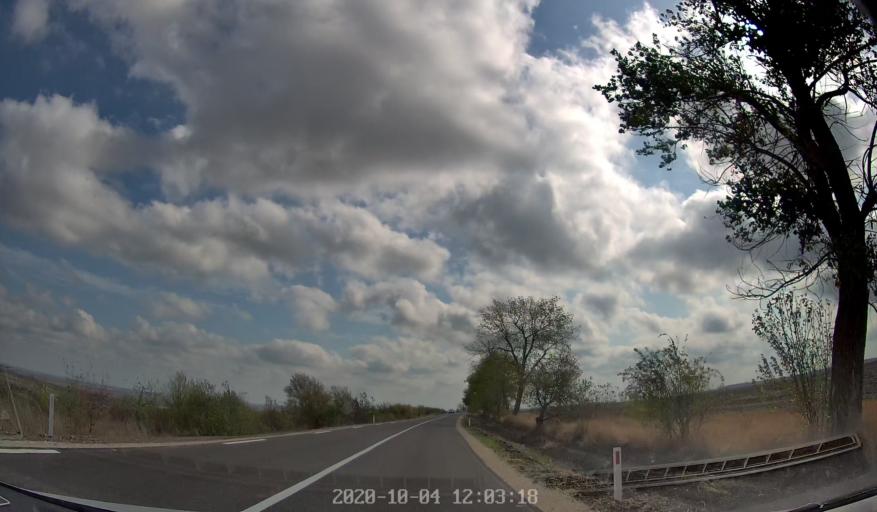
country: MD
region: Rezina
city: Saharna
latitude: 47.6129
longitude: 28.9243
